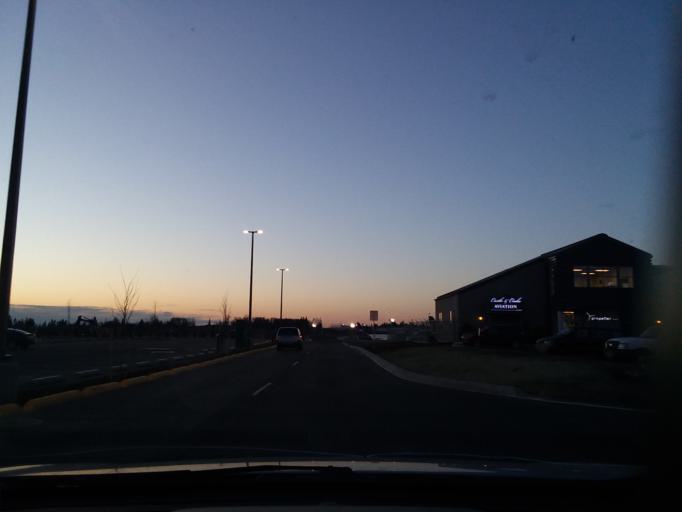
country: US
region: Washington
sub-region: Snohomish County
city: Mukilteo
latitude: 47.9092
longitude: -122.2779
